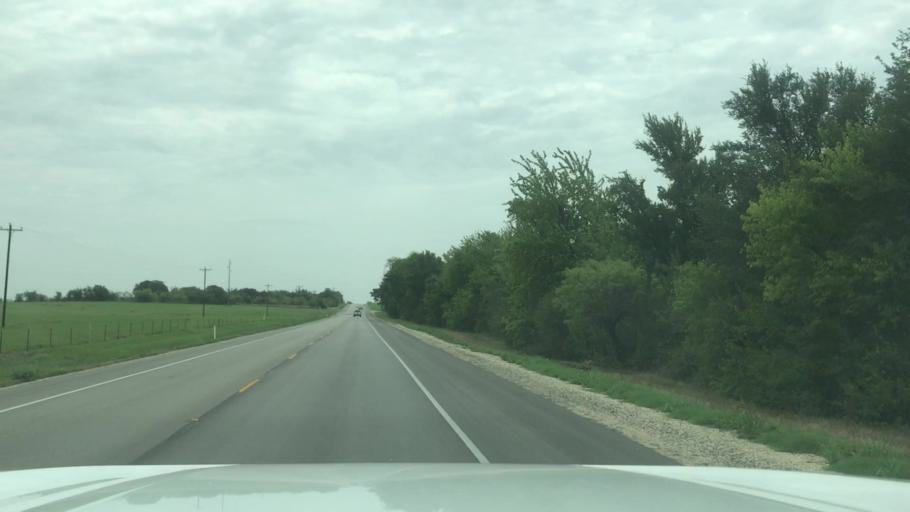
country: US
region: Texas
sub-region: Erath County
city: Dublin
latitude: 32.0895
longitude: -98.2615
